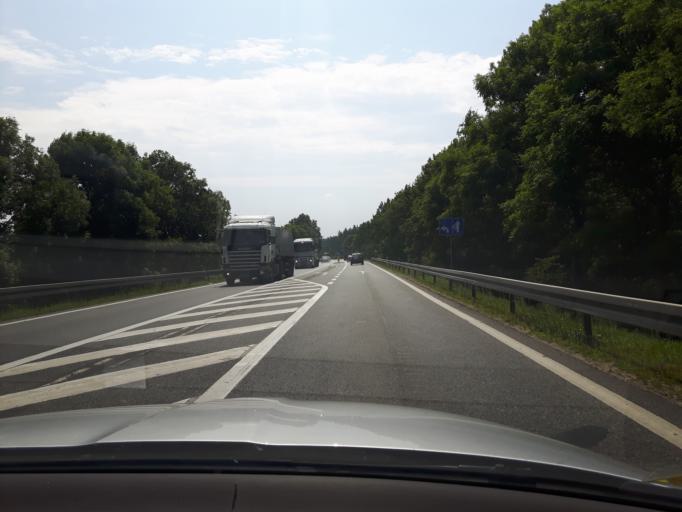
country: PL
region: Masovian Voivodeship
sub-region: Powiat mlawski
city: Mlawa
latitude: 53.1477
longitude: 20.4025
